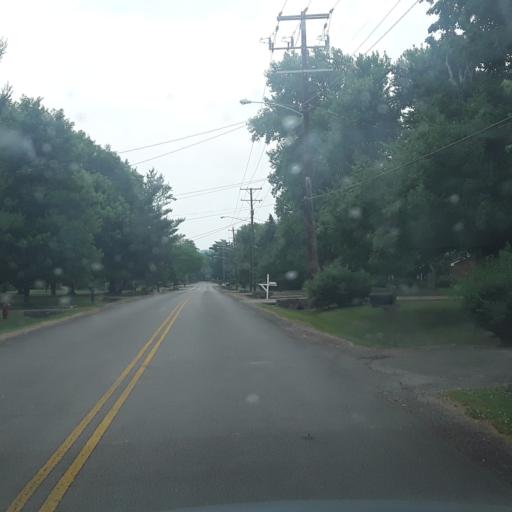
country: US
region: Tennessee
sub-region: Davidson County
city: Oak Hill
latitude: 36.0727
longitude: -86.7456
